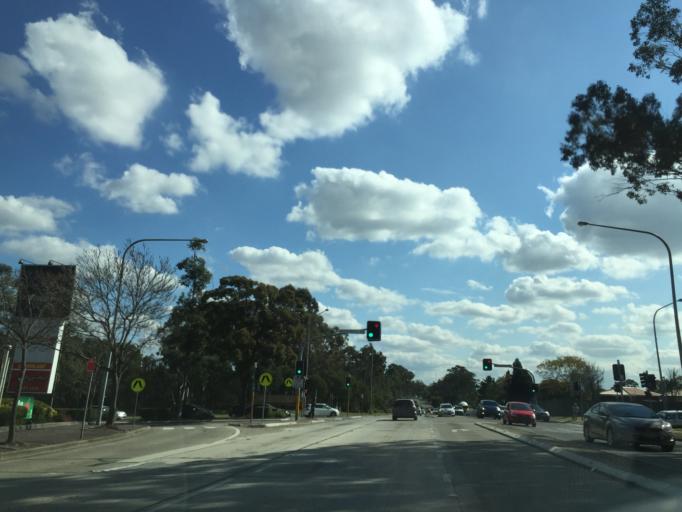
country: AU
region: New South Wales
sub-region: Blacktown
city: Quakers Hill
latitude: -33.7476
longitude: 150.8803
